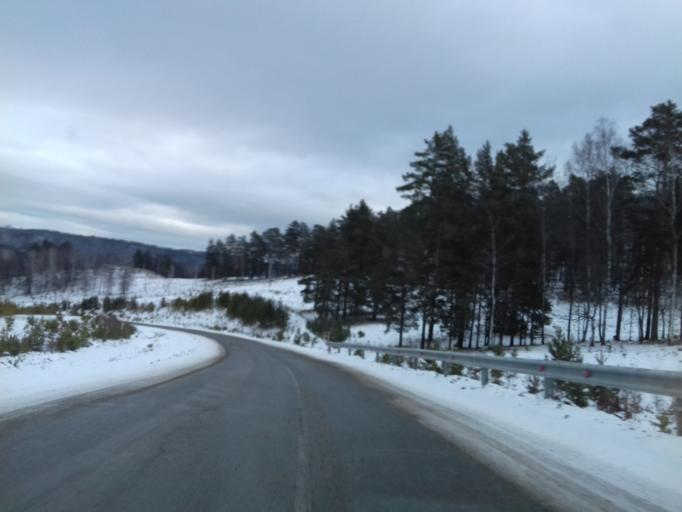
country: RU
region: Bashkortostan
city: Starosubkhangulovo
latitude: 53.2766
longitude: 57.5273
